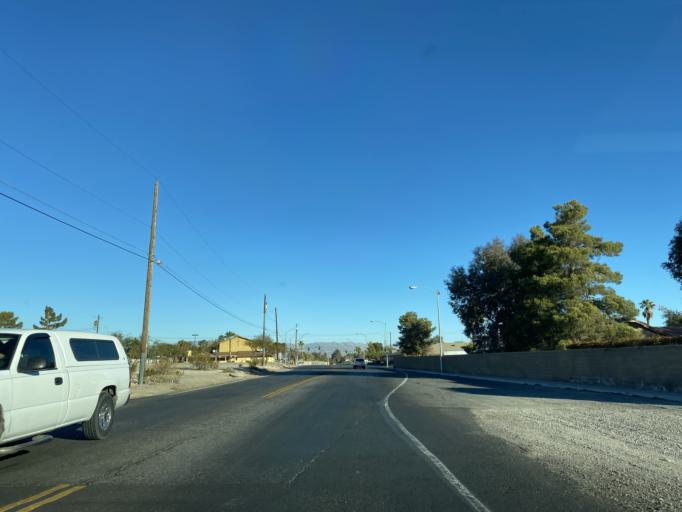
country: US
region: Nevada
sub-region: Clark County
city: Whitney
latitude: 36.0844
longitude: -115.1099
